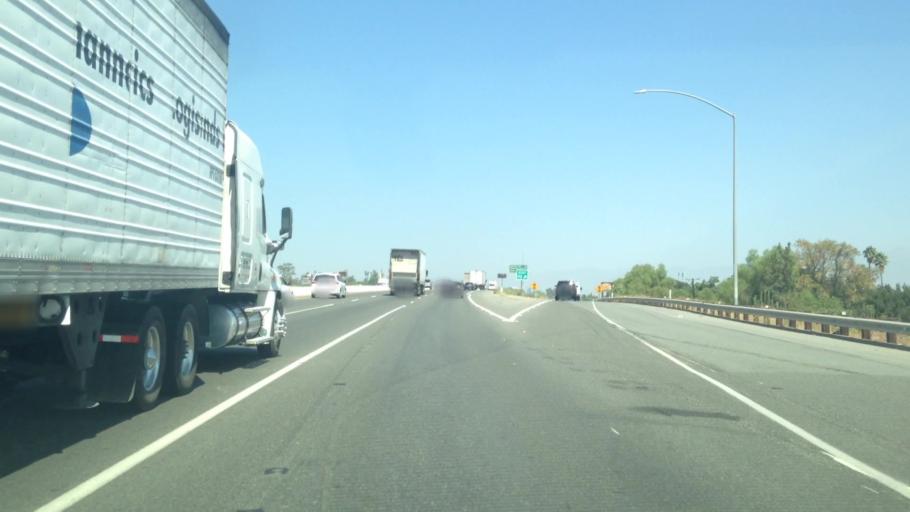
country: US
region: California
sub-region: Riverside County
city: El Cerrito
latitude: 33.8292
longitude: -117.5276
